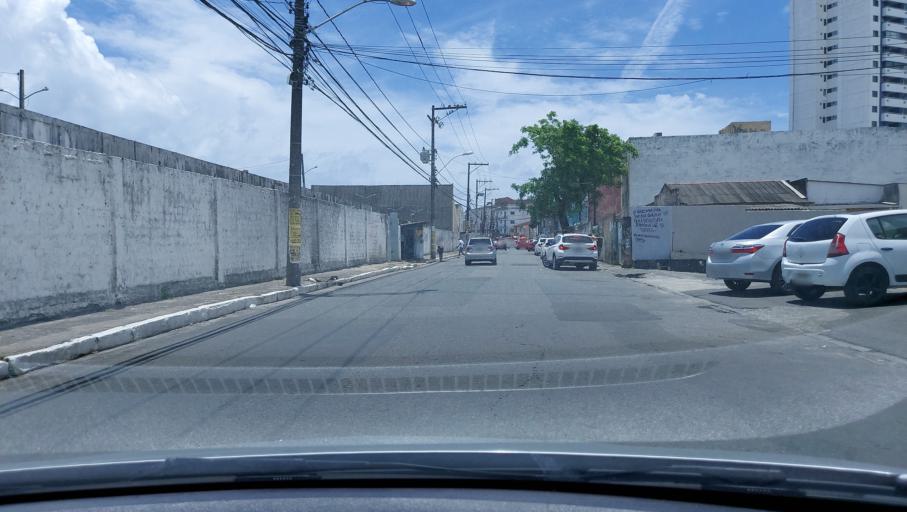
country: BR
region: Bahia
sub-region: Salvador
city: Salvador
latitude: -12.9860
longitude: -38.4782
